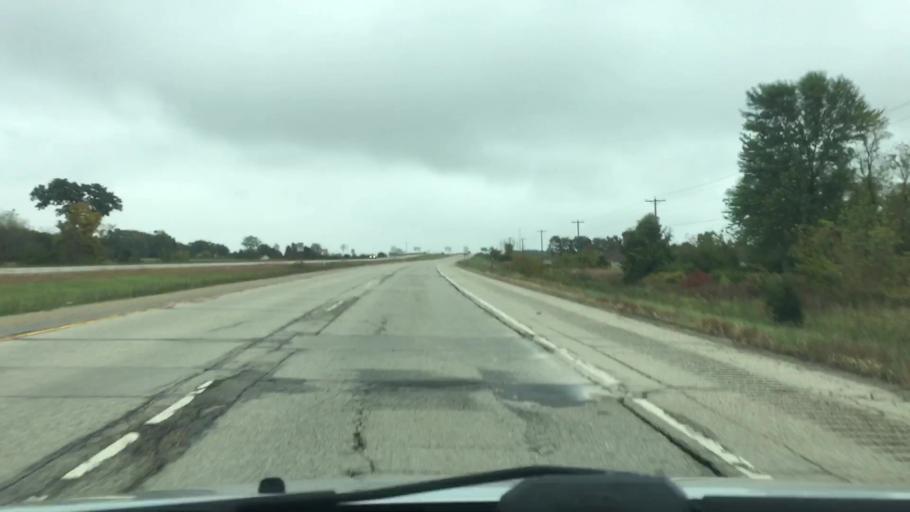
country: US
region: Wisconsin
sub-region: Walworth County
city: Elkhorn
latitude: 42.6887
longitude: -88.5324
